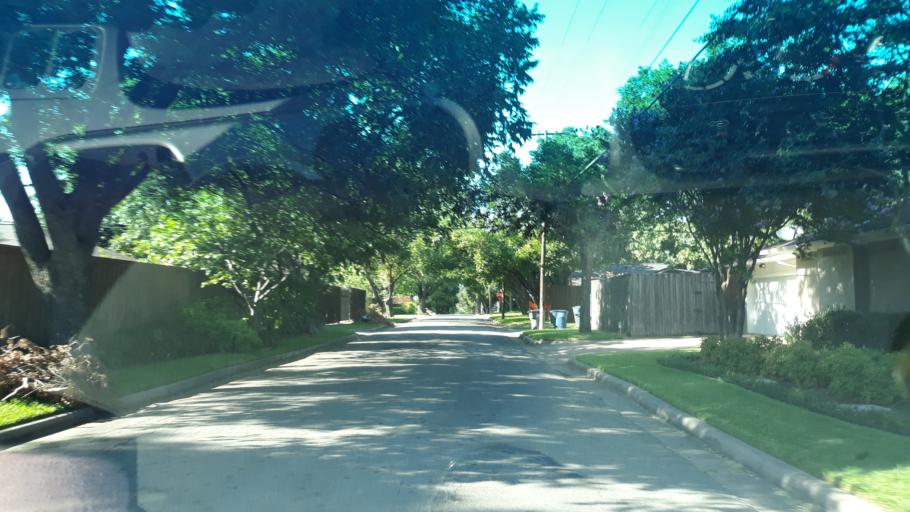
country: US
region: Texas
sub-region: Dallas County
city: Highland Park
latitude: 32.8257
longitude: -96.7560
